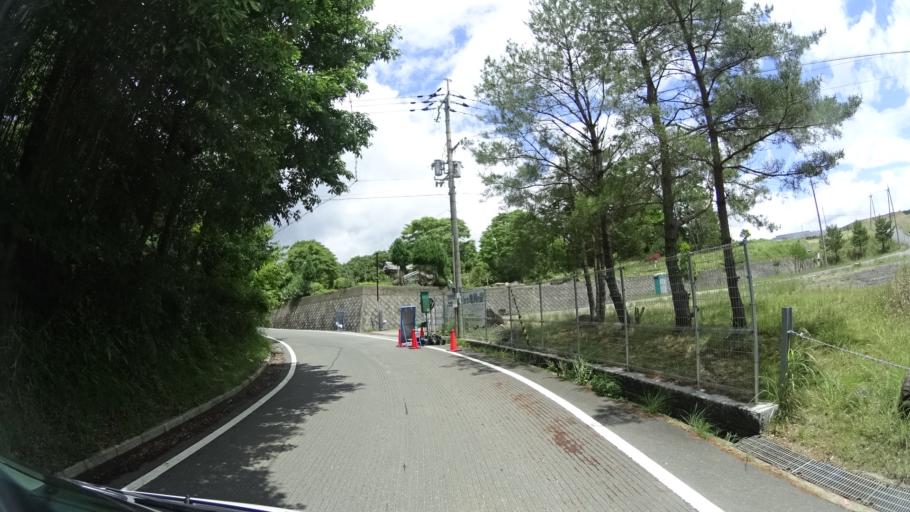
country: JP
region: Hyogo
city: Sasayama
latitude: 35.0265
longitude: 135.3898
